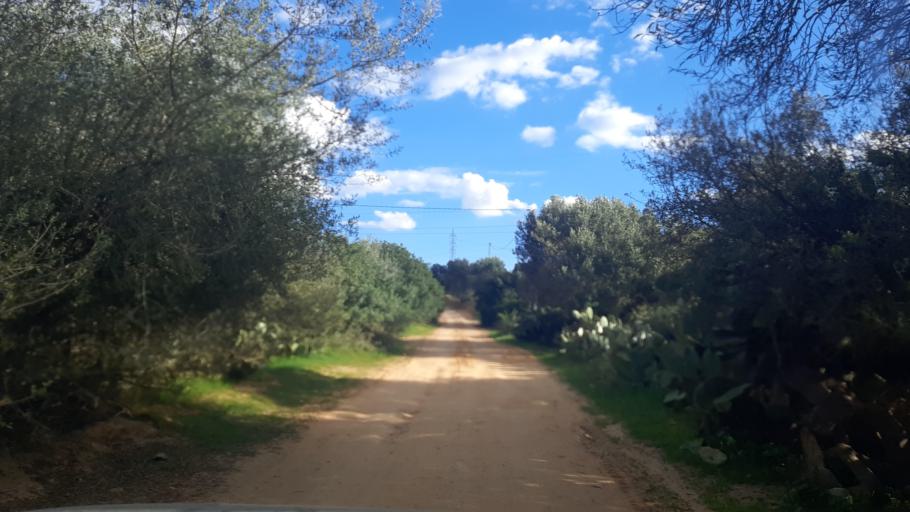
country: TN
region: Nabul
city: Bu `Urqub
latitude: 36.4401
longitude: 10.5081
